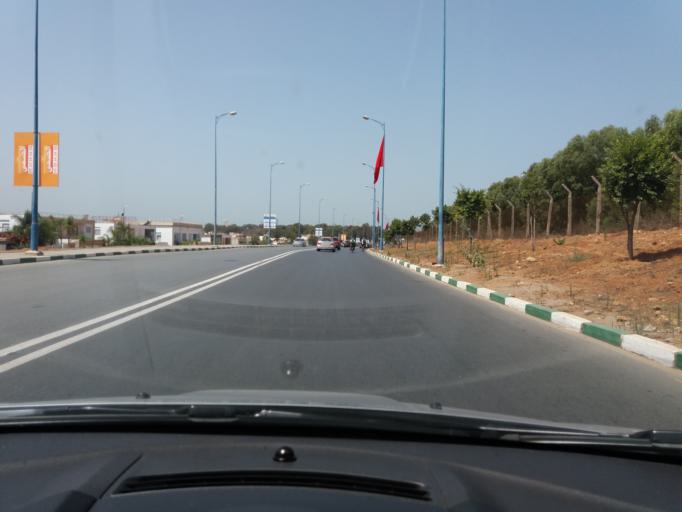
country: MA
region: Gharb-Chrarda-Beni Hssen
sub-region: Kenitra Province
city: Kenitra
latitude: 34.2709
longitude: -6.6361
